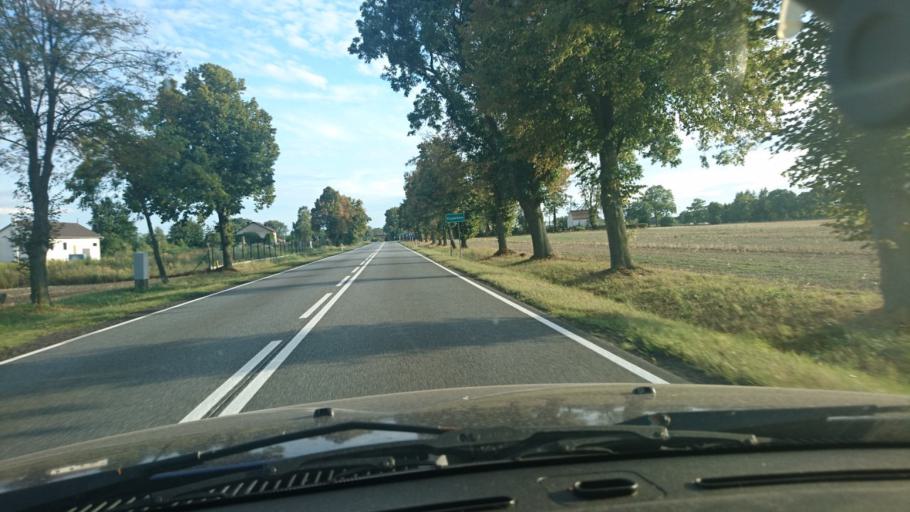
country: PL
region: Opole Voivodeship
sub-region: Powiat kluczborski
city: Kluczbork
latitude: 51.0321
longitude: 18.1928
